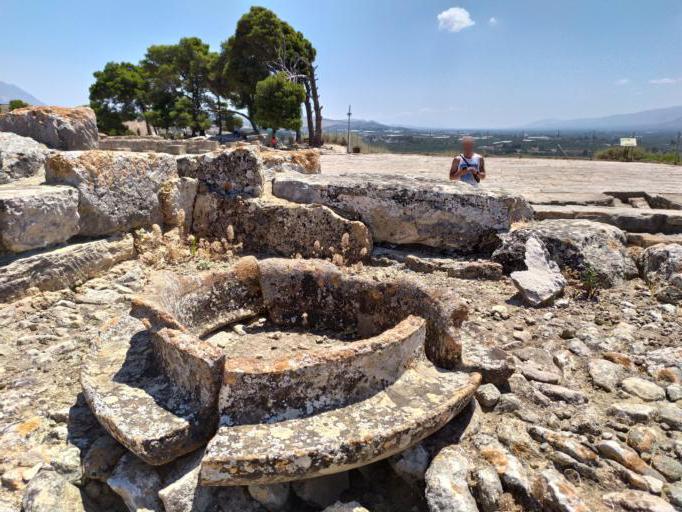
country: GR
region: Crete
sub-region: Nomos Irakleiou
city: Tympaki
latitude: 35.0510
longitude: 24.8143
